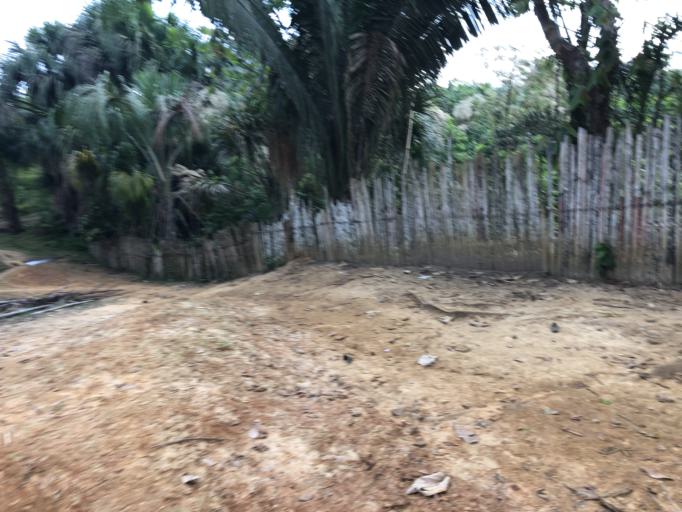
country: PE
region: Loreto
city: Puerto Galilea
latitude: -4.0547
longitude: -77.7615
